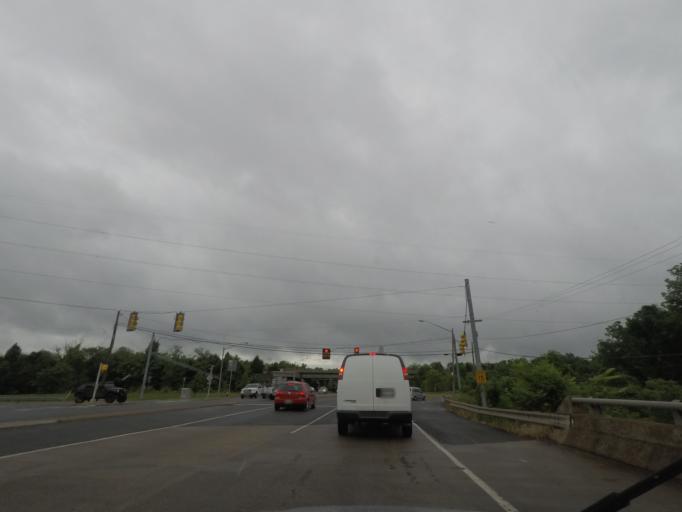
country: US
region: Virginia
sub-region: Loudoun County
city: Leesburg
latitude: 39.1014
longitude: -77.5749
